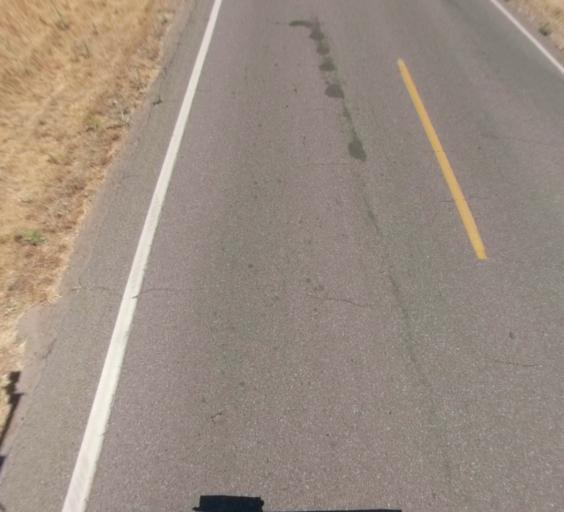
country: US
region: California
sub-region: Madera County
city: Parksdale
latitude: 36.9828
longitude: -120.0196
